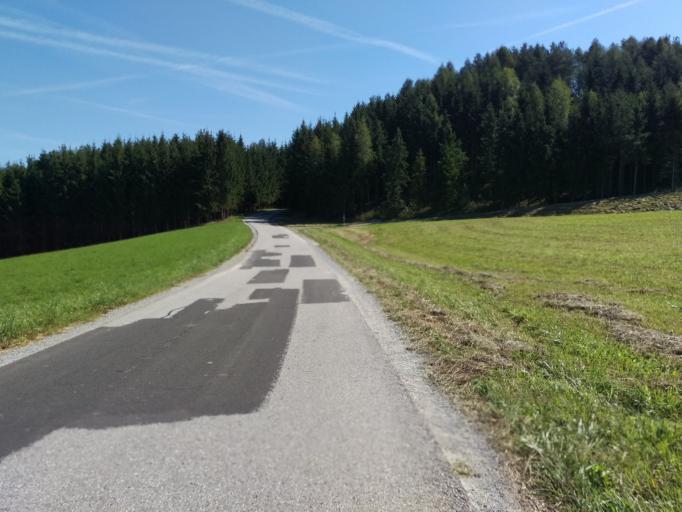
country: AT
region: Styria
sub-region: Politischer Bezirk Graz-Umgebung
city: Nestelbach bei Graz
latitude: 47.0624
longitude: 15.5770
